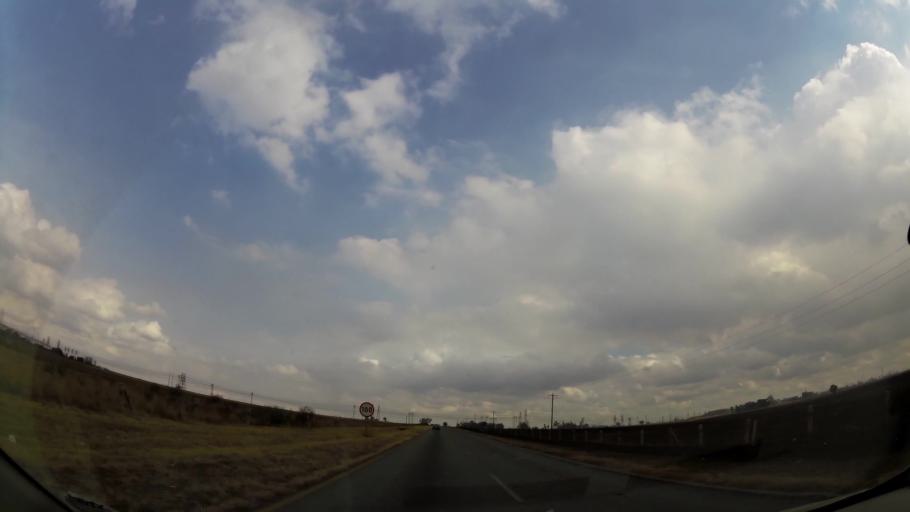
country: ZA
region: Orange Free State
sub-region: Fezile Dabi District Municipality
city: Sasolburg
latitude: -26.8173
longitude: 27.9065
